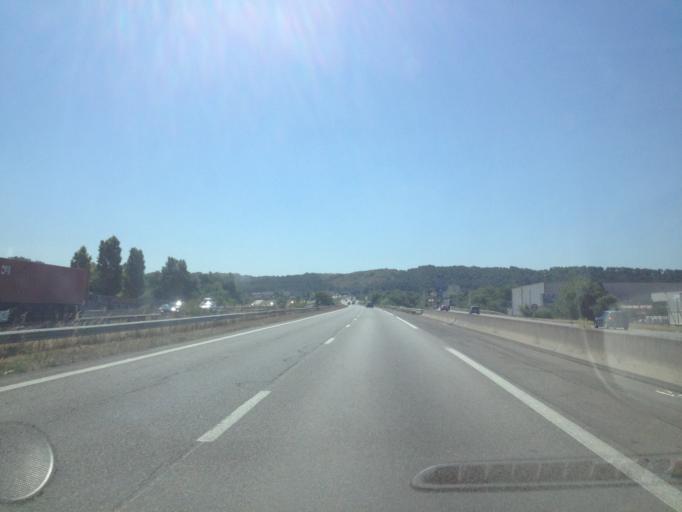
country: FR
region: Provence-Alpes-Cote d'Azur
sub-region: Departement des Bouches-du-Rhone
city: Saint-Victoret
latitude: 43.4203
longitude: 5.2702
